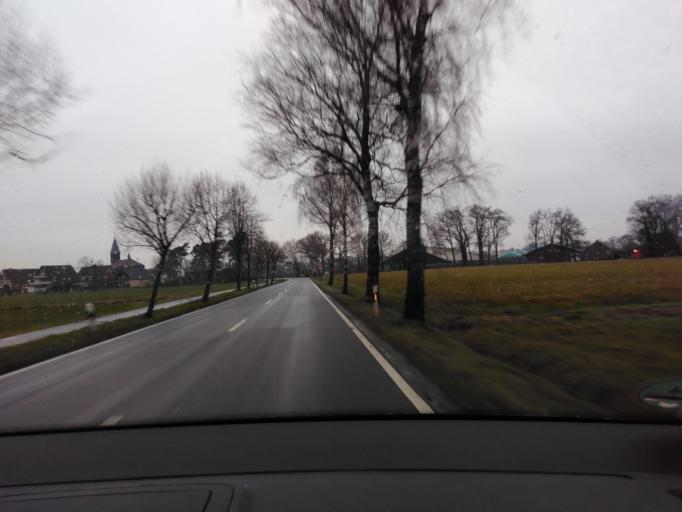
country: DE
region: North Rhine-Westphalia
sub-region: Regierungsbezirk Detmold
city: Verl
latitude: 51.8928
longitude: 8.4781
